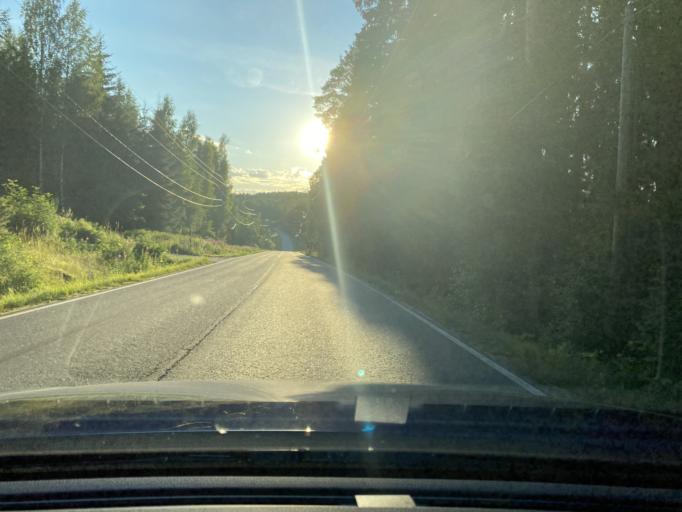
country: FI
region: Uusimaa
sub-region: Helsinki
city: Nurmijaervi
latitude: 60.4084
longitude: 24.7800
